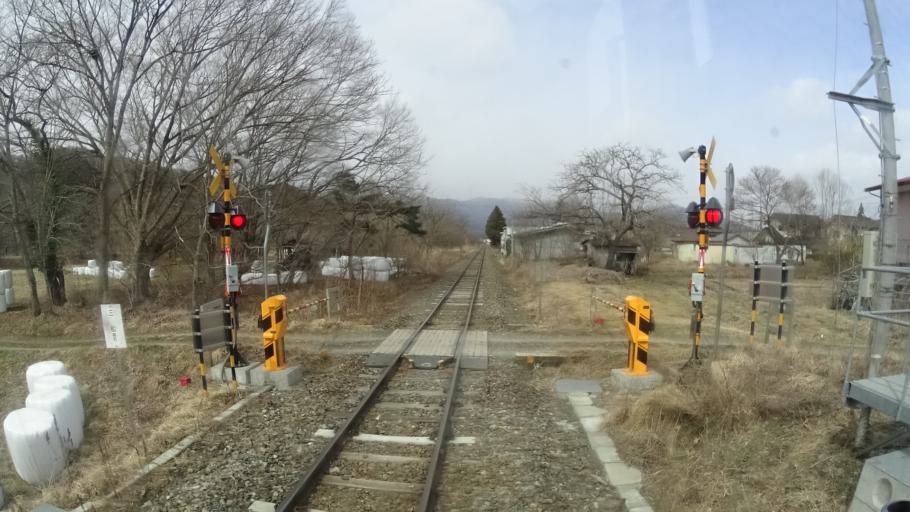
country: JP
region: Iwate
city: Tono
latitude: 39.3214
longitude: 141.5594
